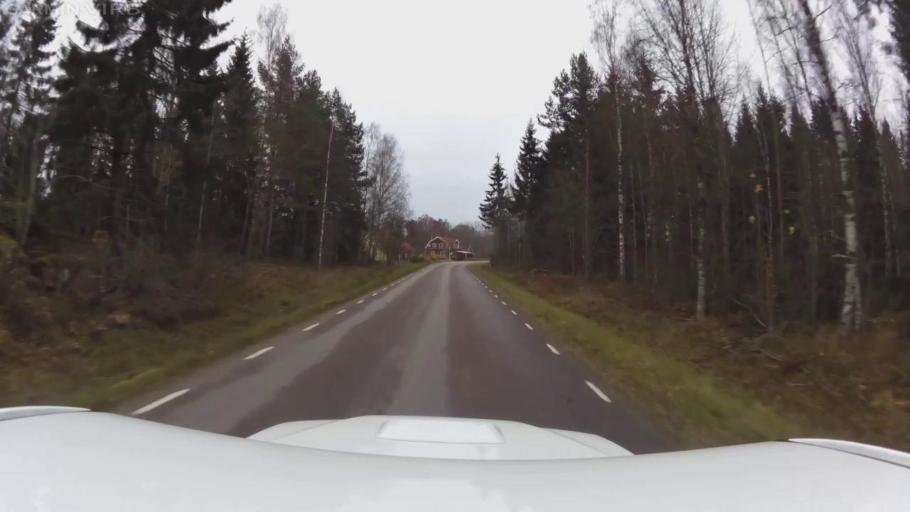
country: SE
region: OEstergoetland
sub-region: Linkopings Kommun
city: Vikingstad
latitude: 58.2333
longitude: 15.3932
